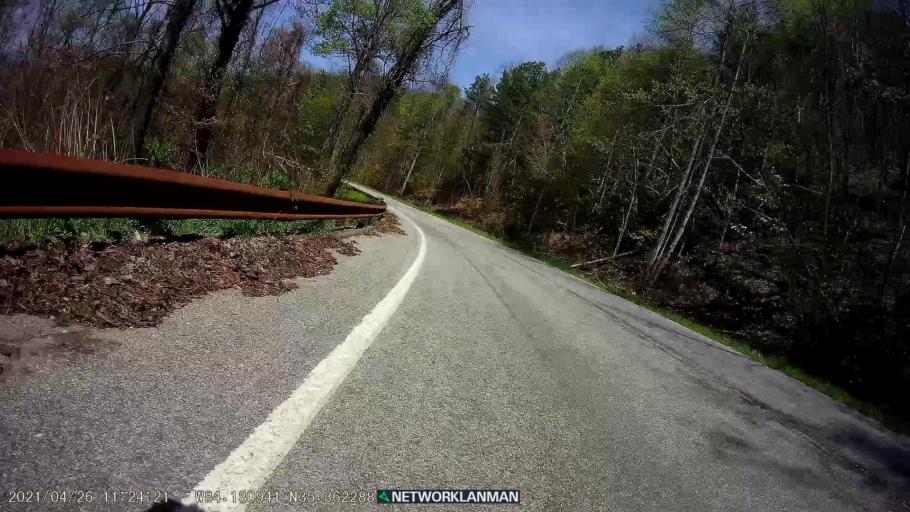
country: US
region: Tennessee
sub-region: Monroe County
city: Vonore
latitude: 35.3622
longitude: -84.1310
